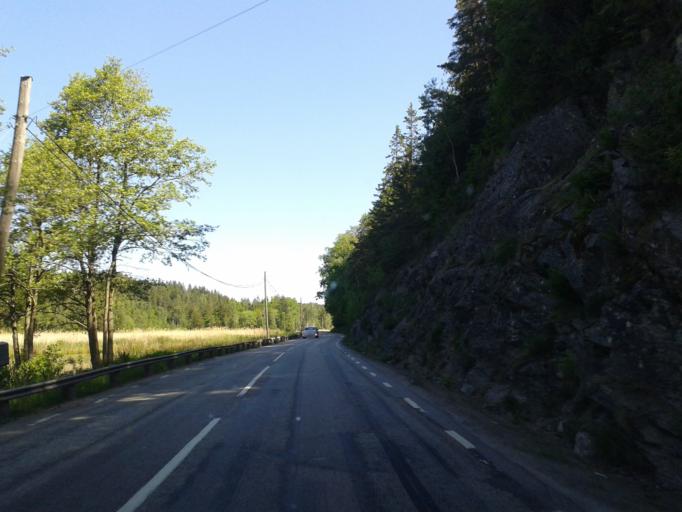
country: SE
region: Vaestra Goetaland
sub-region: Orust
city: Henan
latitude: 58.2326
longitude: 11.6935
